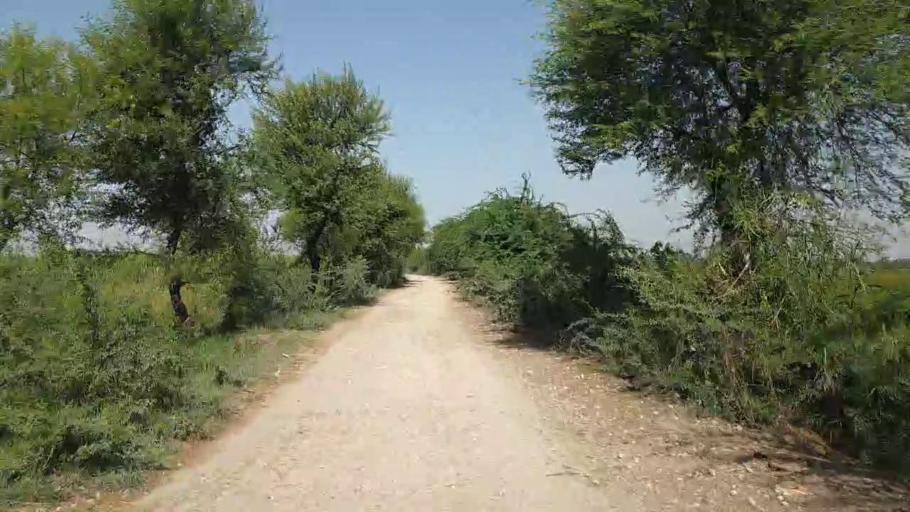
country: PK
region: Sindh
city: Tando Bago
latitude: 24.7573
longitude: 69.0247
